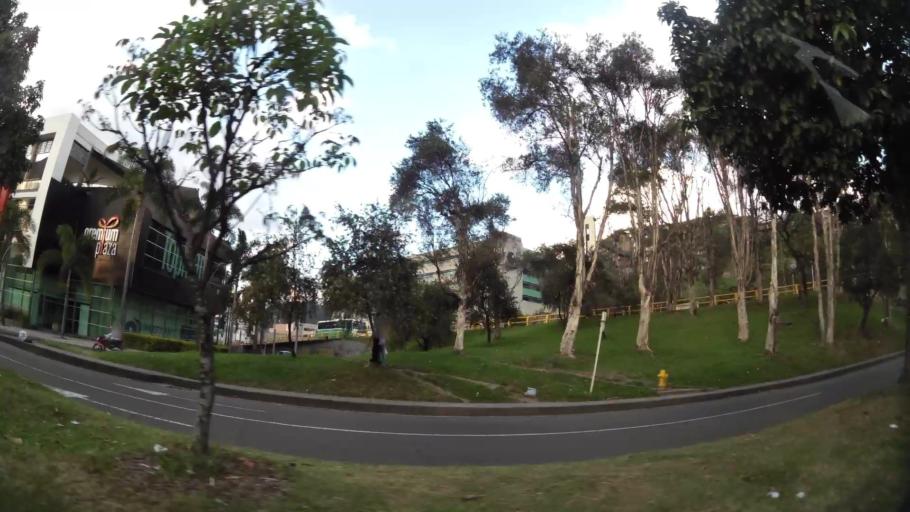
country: CO
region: Antioquia
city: Medellin
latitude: 6.2279
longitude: -75.5699
